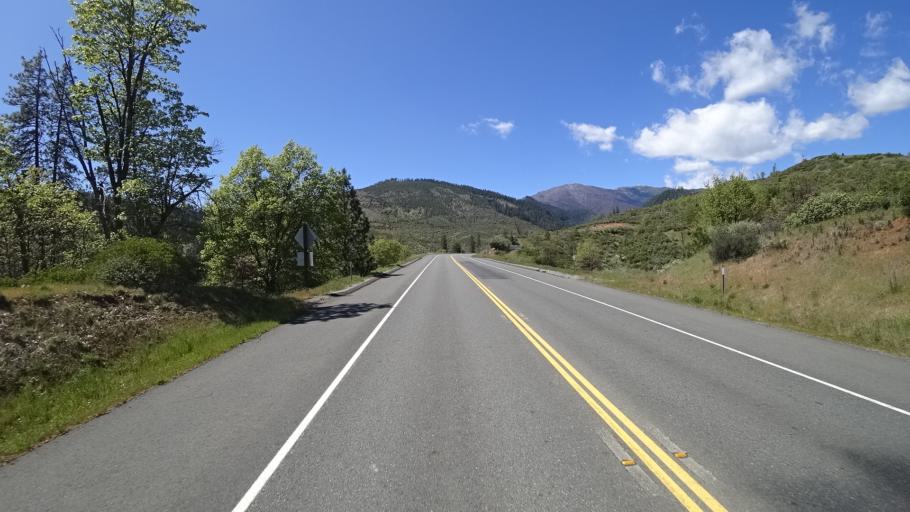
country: US
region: California
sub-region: Trinity County
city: Weaverville
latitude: 40.7369
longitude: -122.9647
